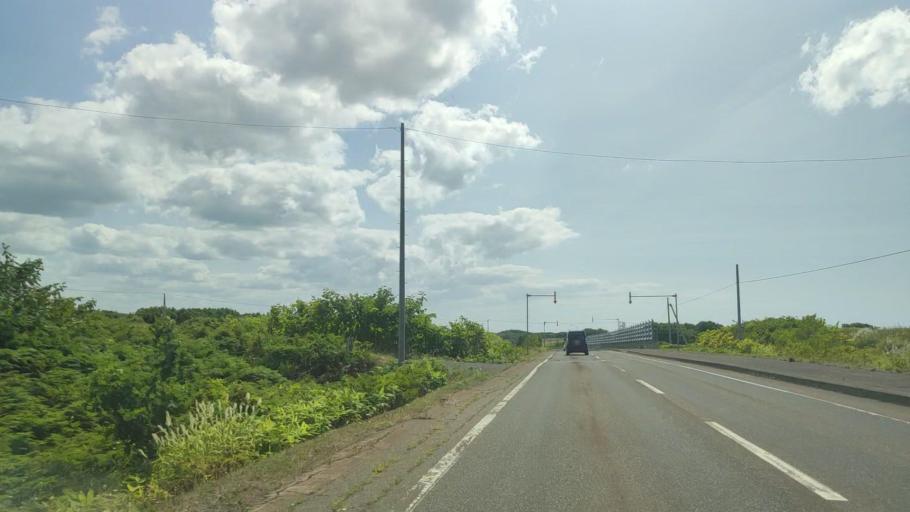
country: JP
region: Hokkaido
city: Makubetsu
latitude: 44.7878
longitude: 141.7902
